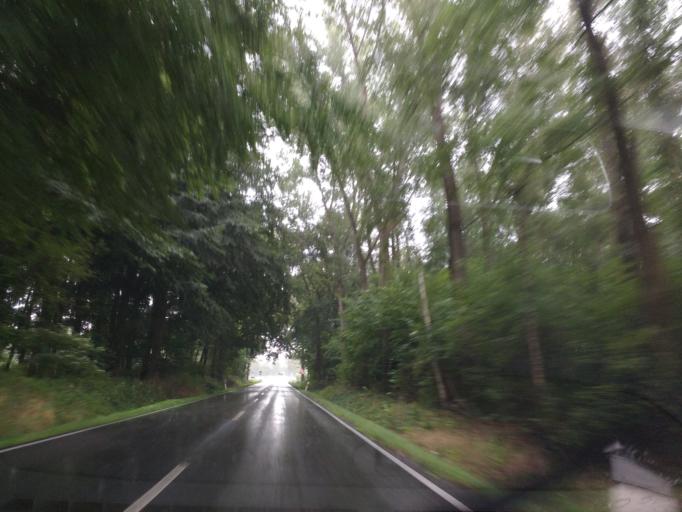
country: DE
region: North Rhine-Westphalia
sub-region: Regierungsbezirk Munster
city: Lienen
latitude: 52.1076
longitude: 7.9494
